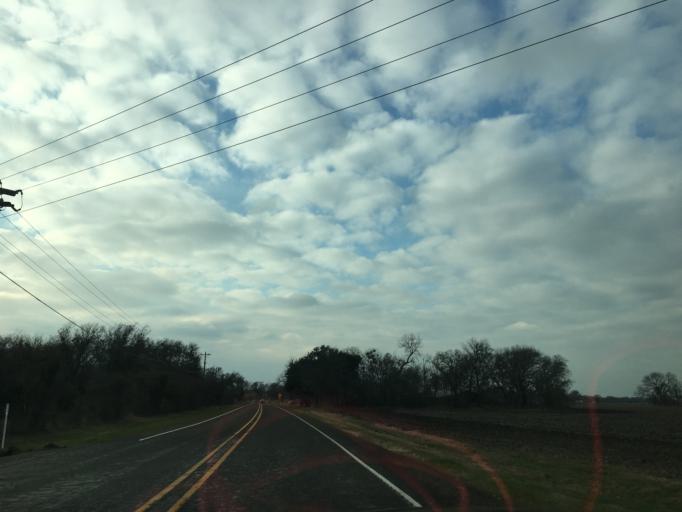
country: US
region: Texas
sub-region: Ellis County
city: Palmer
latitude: 32.4544
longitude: -96.7389
